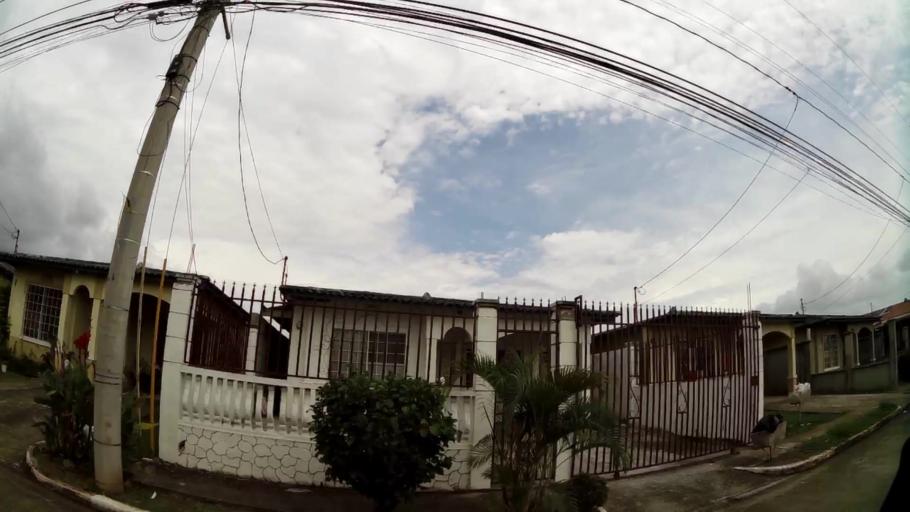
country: PA
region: Panama
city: Tocumen
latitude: 9.0422
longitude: -79.4053
